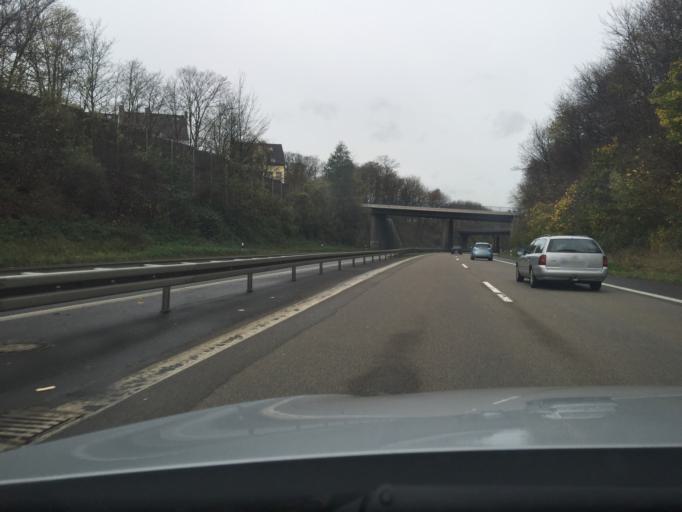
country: DE
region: North Rhine-Westphalia
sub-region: Regierungsbezirk Dusseldorf
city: Velbert
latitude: 51.3463
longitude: 7.0486
